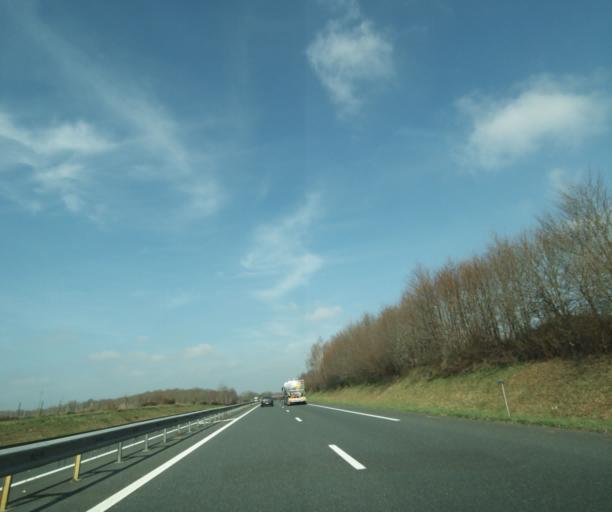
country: FR
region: Centre
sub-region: Departement de l'Indre
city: Chantome
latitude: 46.3912
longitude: 1.4504
